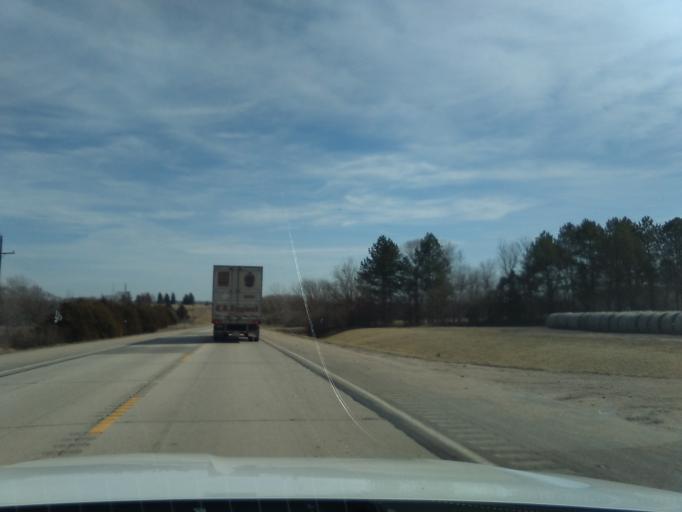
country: US
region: Nebraska
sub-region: Lancaster County
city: Hickman
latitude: 40.6539
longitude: -96.7573
